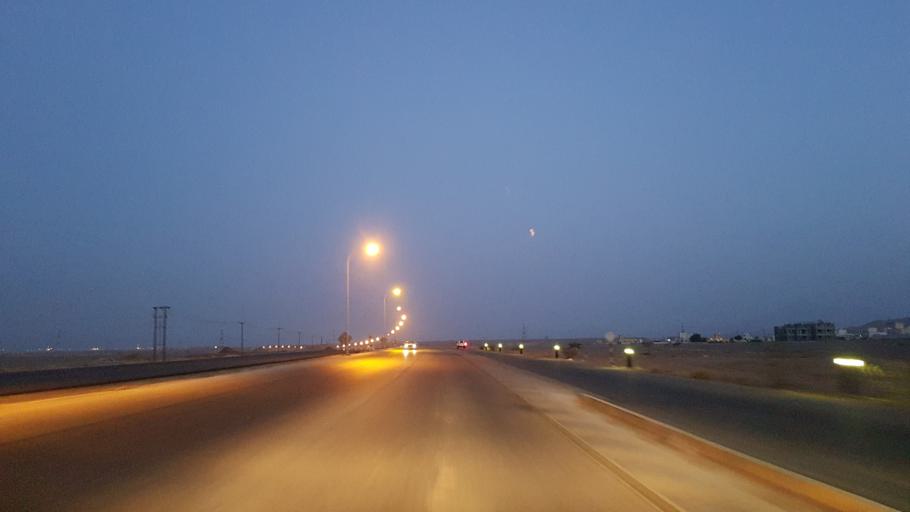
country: OM
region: Ash Sharqiyah
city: Sur
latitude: 22.5937
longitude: 59.4370
